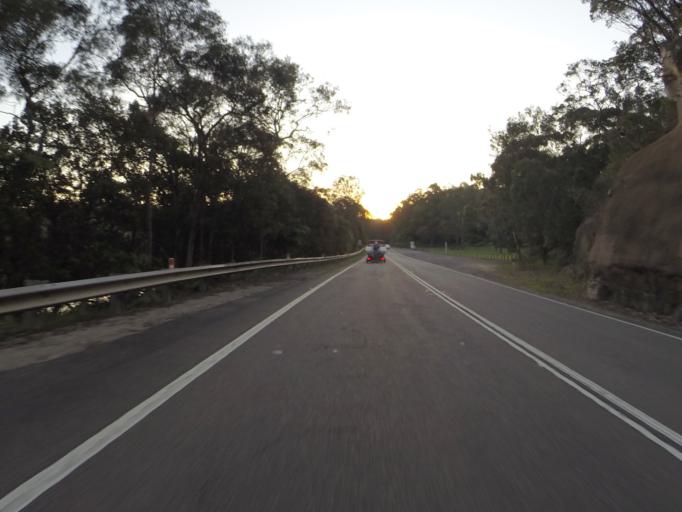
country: AU
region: New South Wales
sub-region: Bankstown
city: Padstow
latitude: -33.9730
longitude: 151.0215
